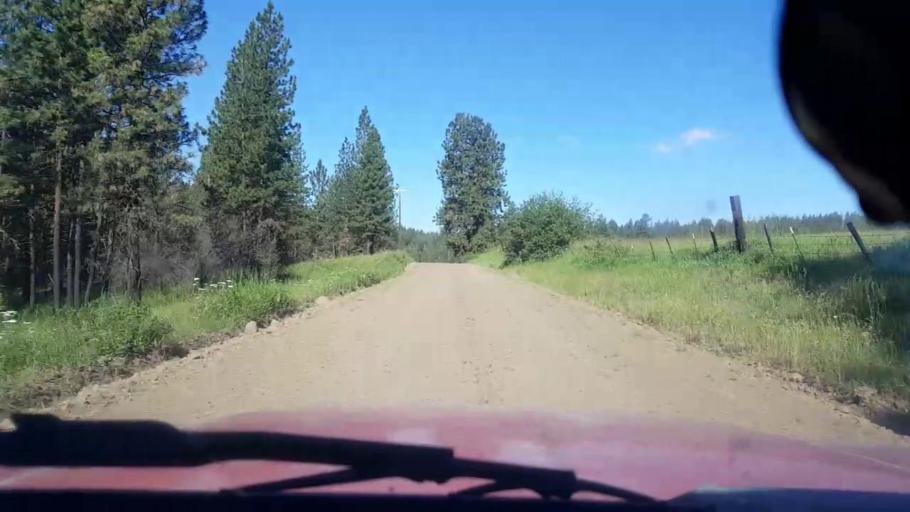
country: US
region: Washington
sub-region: Garfield County
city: Pomeroy
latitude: 45.9845
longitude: -117.4766
